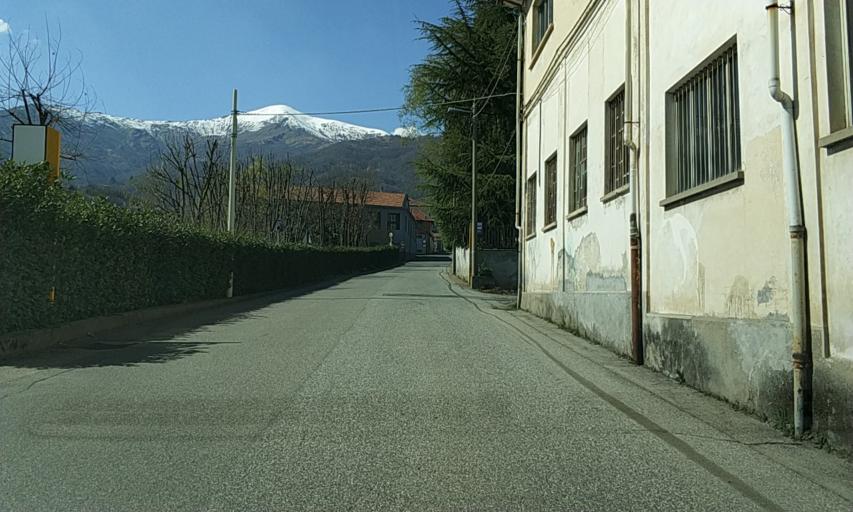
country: IT
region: Piedmont
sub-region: Provincia di Torino
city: Forno Canavese
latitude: 45.3431
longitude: 7.5917
